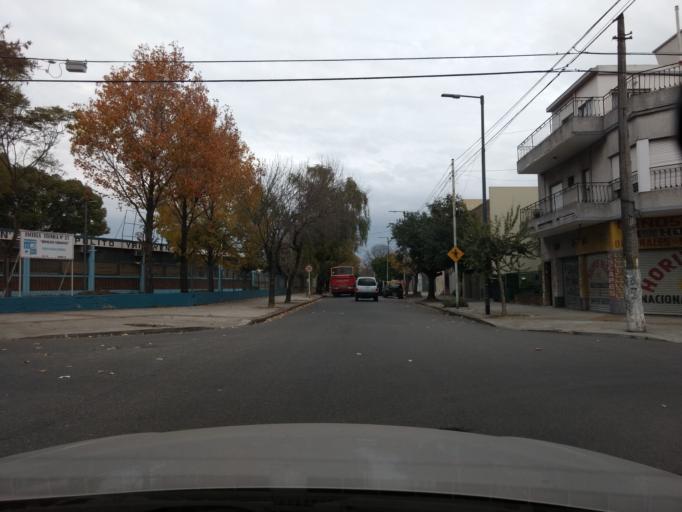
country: AR
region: Buenos Aires F.D.
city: Villa Santa Rita
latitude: -34.6210
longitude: -58.5179
